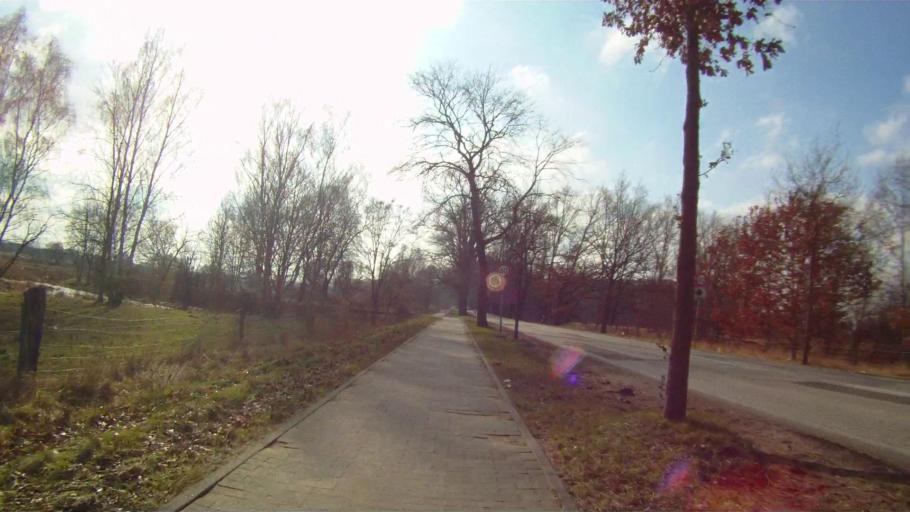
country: DE
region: Brandenburg
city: Erkner
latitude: 52.4065
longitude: 13.7495
